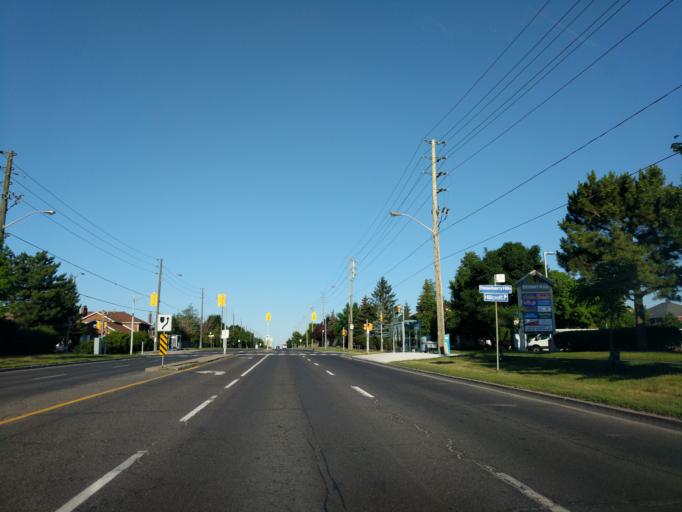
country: CA
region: Ontario
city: Markham
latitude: 43.8301
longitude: -79.2796
